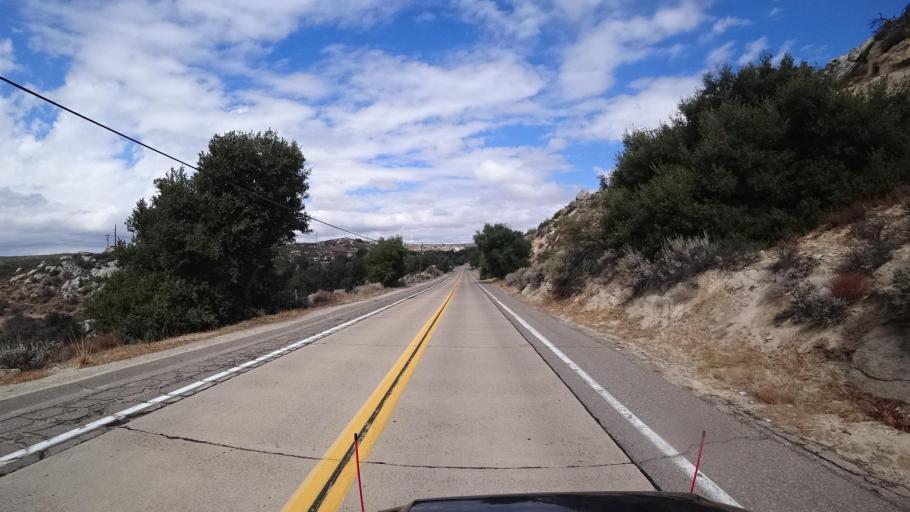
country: US
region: California
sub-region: San Diego County
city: Campo
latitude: 32.6778
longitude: -116.3322
